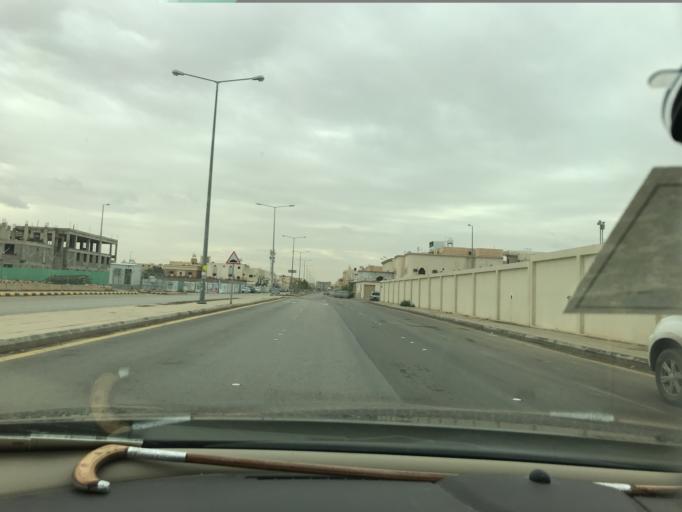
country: SA
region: Ar Riyad
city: Riyadh
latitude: 24.7550
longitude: 46.8290
